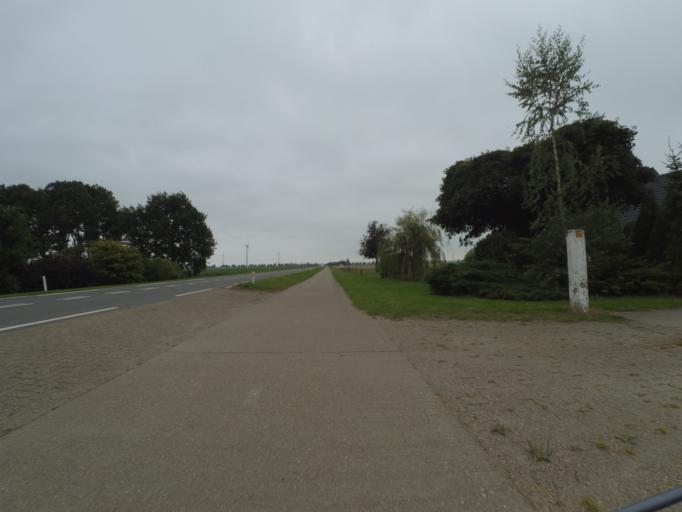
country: NL
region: Flevoland
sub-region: Gemeente Zeewolde
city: Zeewolde
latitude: 52.3774
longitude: 5.4531
